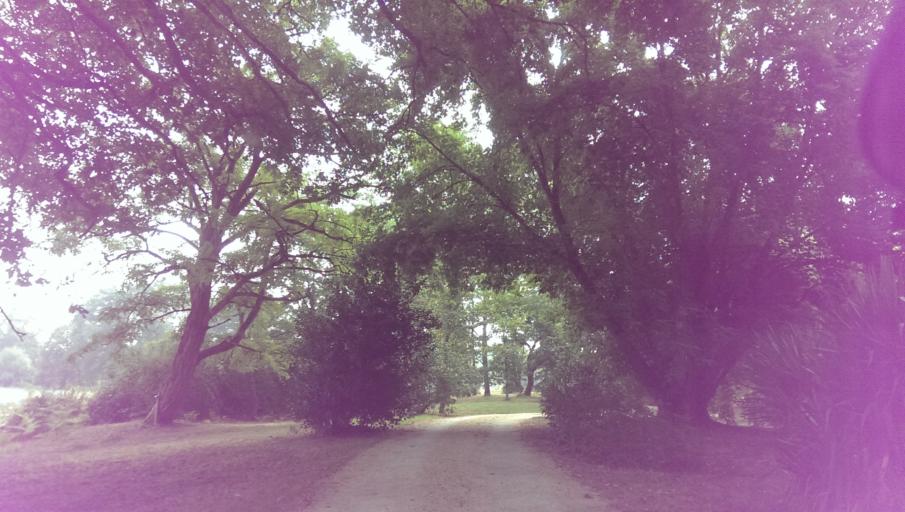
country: FR
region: Aquitaine
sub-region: Departement des Landes
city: Sarbazan
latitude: 44.0945
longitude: -0.1503
